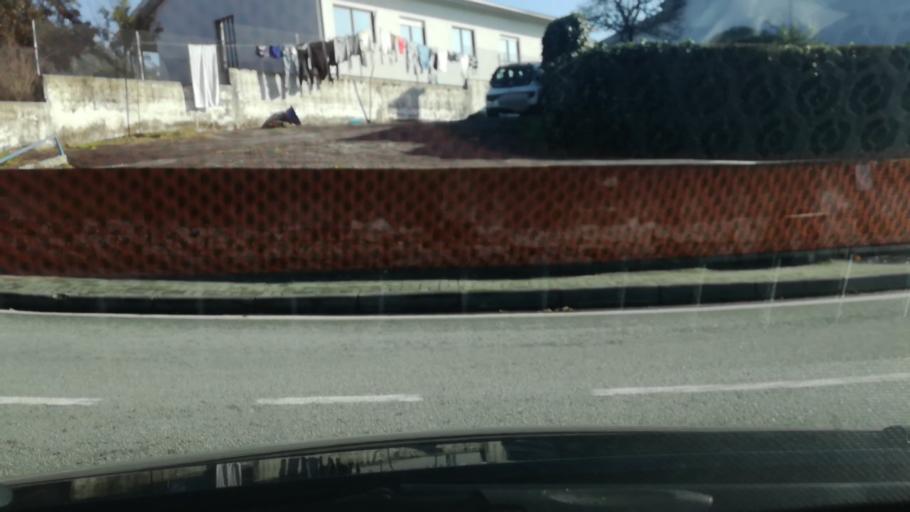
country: PT
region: Braga
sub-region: Guimaraes
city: Ponte
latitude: 41.5227
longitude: -8.3248
